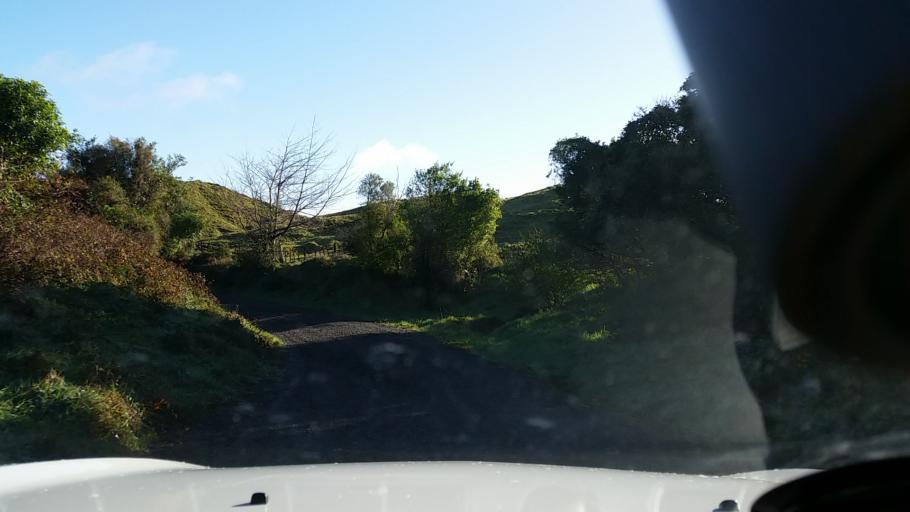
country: NZ
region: Bay of Plenty
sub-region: Kawerau District
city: Kawerau
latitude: -38.0144
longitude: 176.5761
